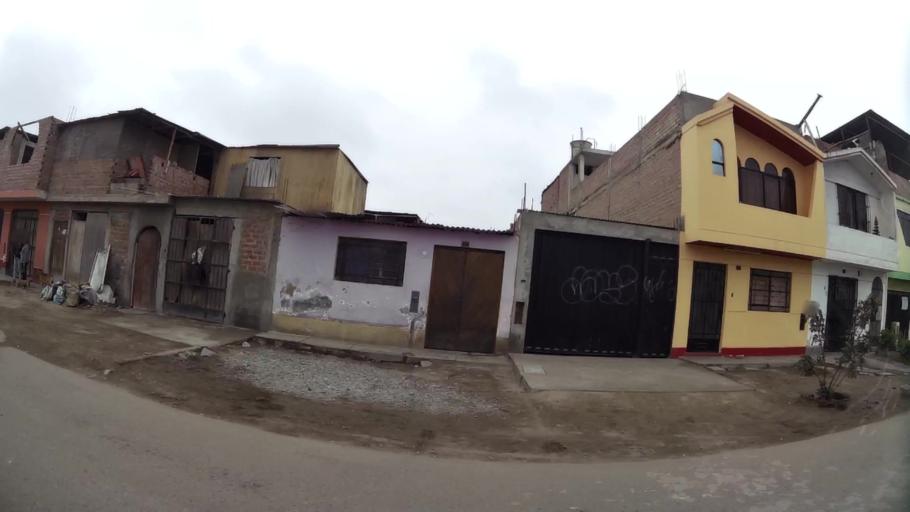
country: PE
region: Lima
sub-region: Lima
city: Punta Hermosa
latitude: -12.2348
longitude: -76.9093
